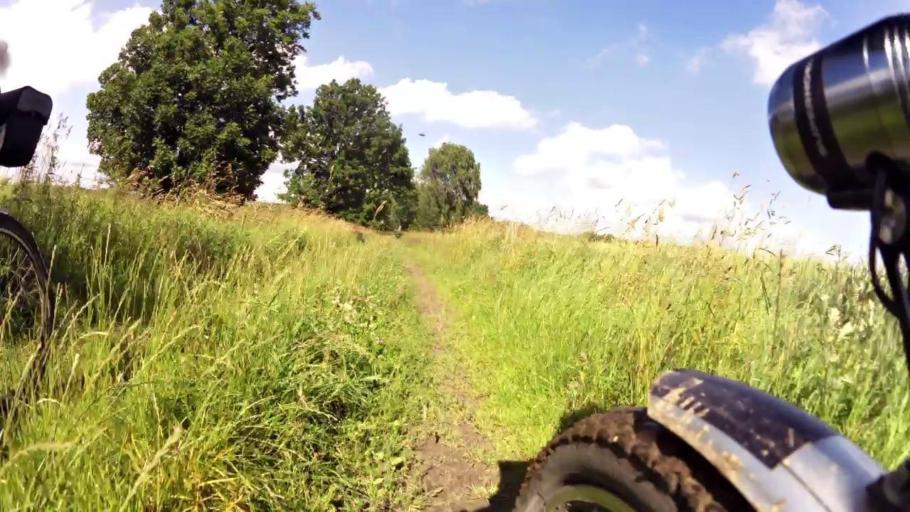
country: PL
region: West Pomeranian Voivodeship
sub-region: Powiat swidwinski
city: Swidwin
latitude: 53.7331
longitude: 15.7487
